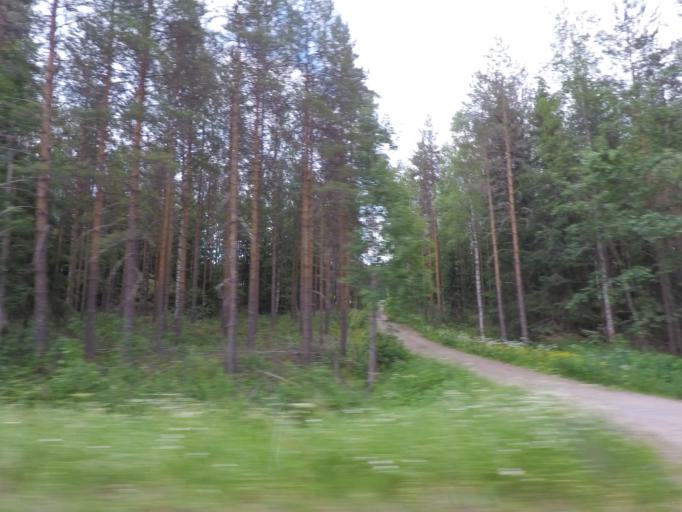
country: FI
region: Paijanne Tavastia
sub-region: Lahti
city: Hollola
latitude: 60.8161
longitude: 25.4829
